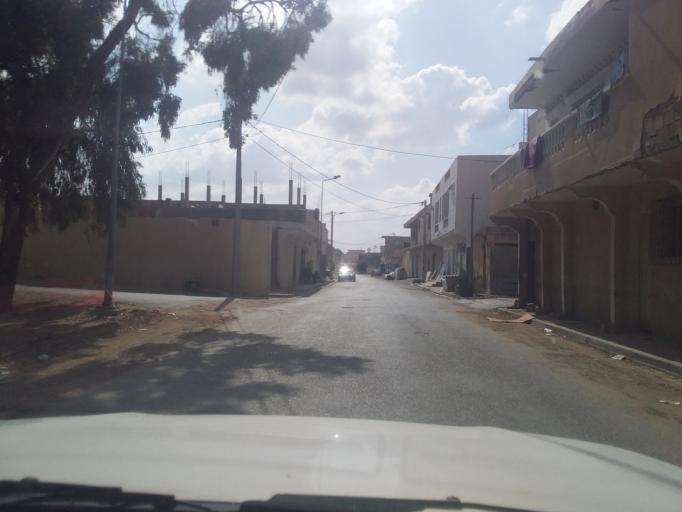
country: TN
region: Qabis
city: Gabes
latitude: 33.6220
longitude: 10.2798
